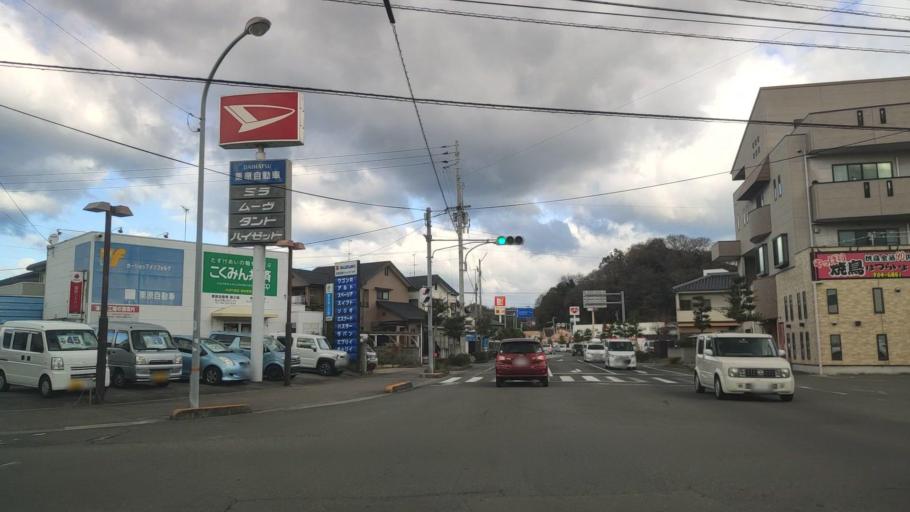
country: JP
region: Ehime
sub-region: Shikoku-chuo Shi
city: Matsuyama
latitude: 33.8664
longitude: 132.7250
